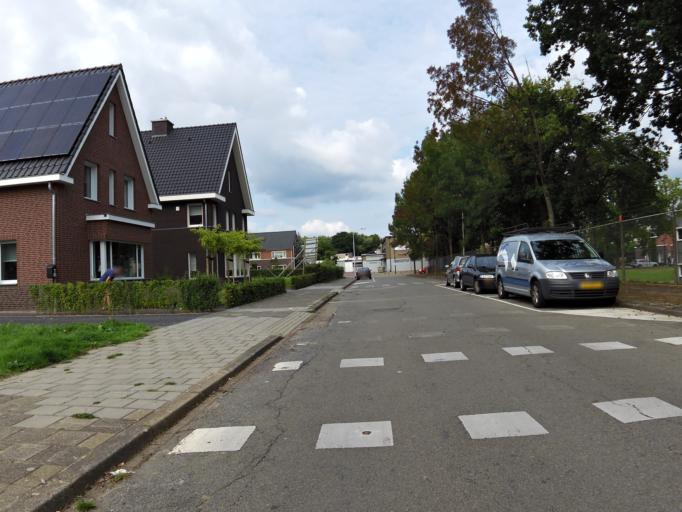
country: NL
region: Limburg
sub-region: Gemeente Kerkrade
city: Kerkrade
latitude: 50.8658
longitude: 6.0754
